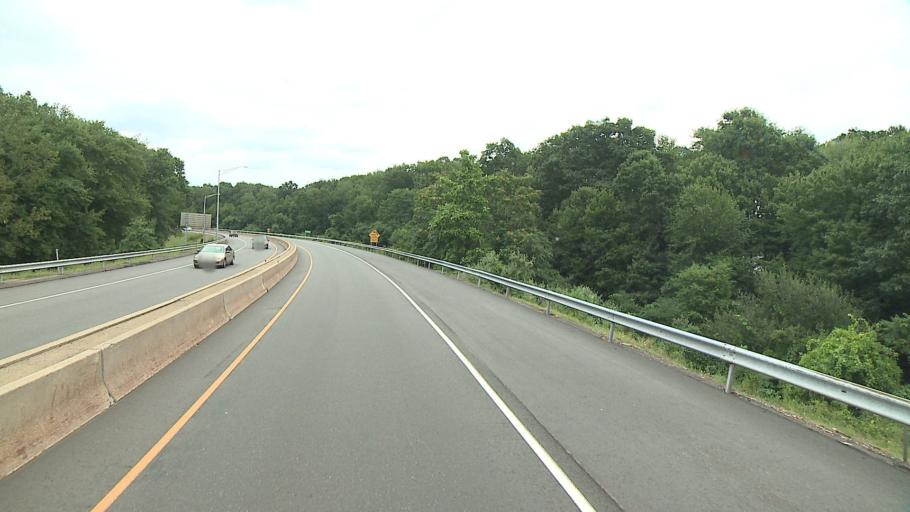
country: US
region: Connecticut
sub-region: Hartford County
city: Glastonbury
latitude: 41.7274
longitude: -72.6104
